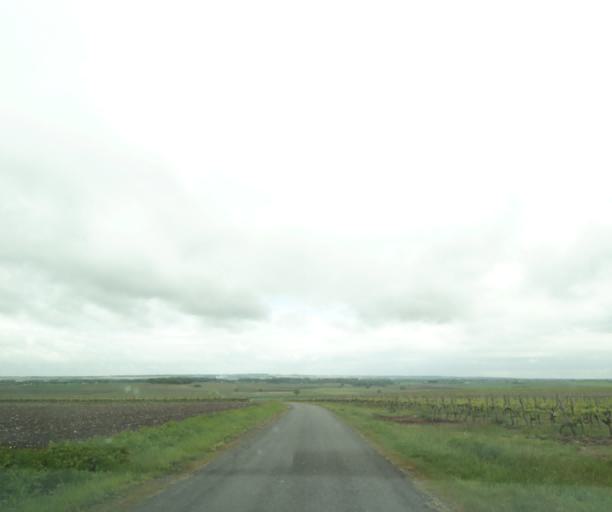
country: FR
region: Poitou-Charentes
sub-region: Departement de la Charente-Maritime
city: Perignac
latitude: 45.6634
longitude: -0.5020
